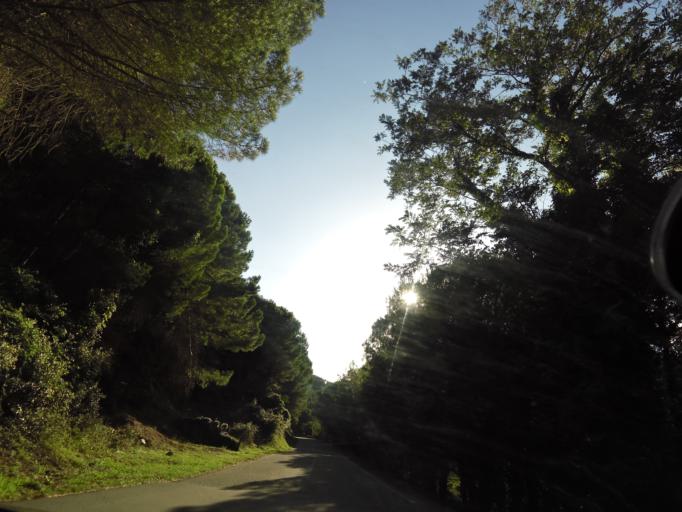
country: IT
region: Calabria
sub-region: Provincia di Reggio Calabria
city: Pazzano
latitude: 38.4639
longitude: 16.4271
